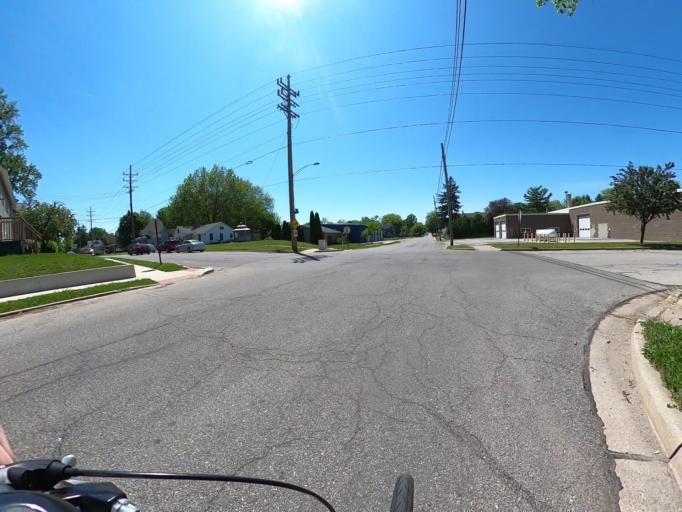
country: US
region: Indiana
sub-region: LaPorte County
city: LaPorte
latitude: 41.6058
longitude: -86.7322
